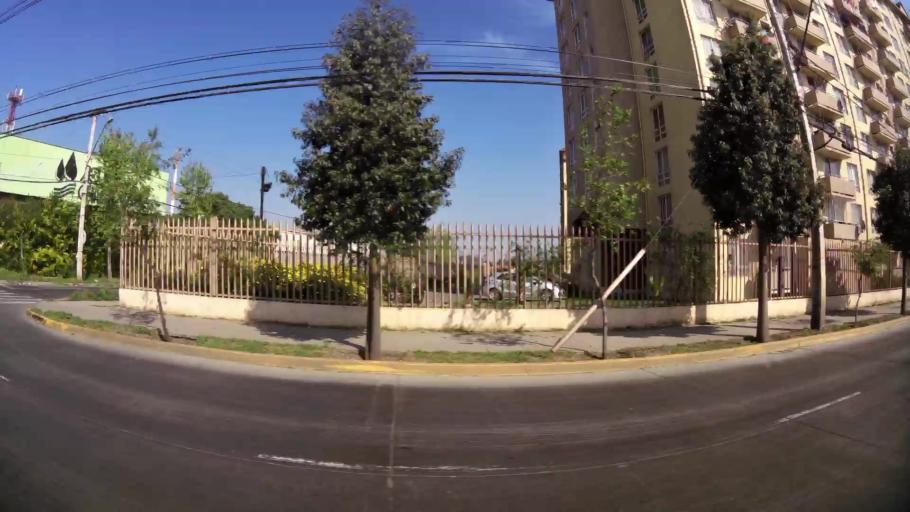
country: CL
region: Santiago Metropolitan
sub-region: Provincia de Santiago
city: Lo Prado
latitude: -33.4564
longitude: -70.7387
